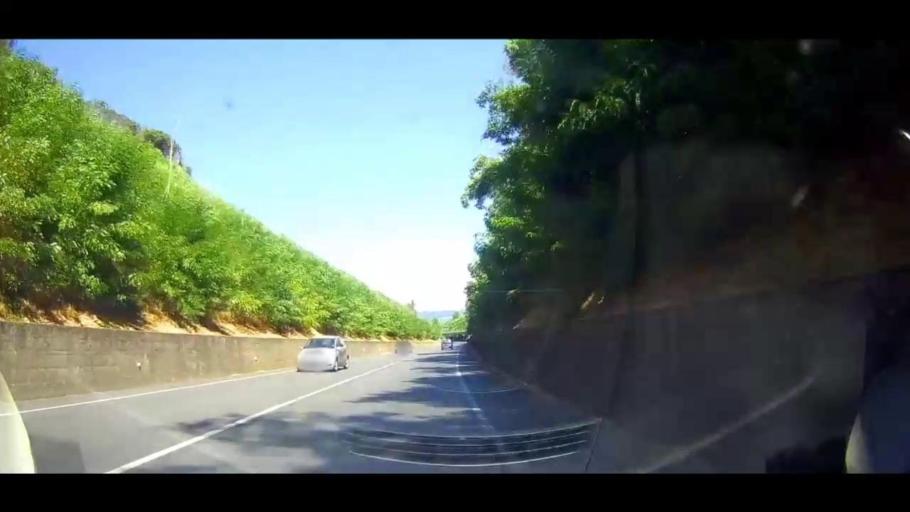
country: IT
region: Calabria
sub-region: Provincia di Cosenza
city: Zumpano
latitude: 39.2985
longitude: 16.2933
